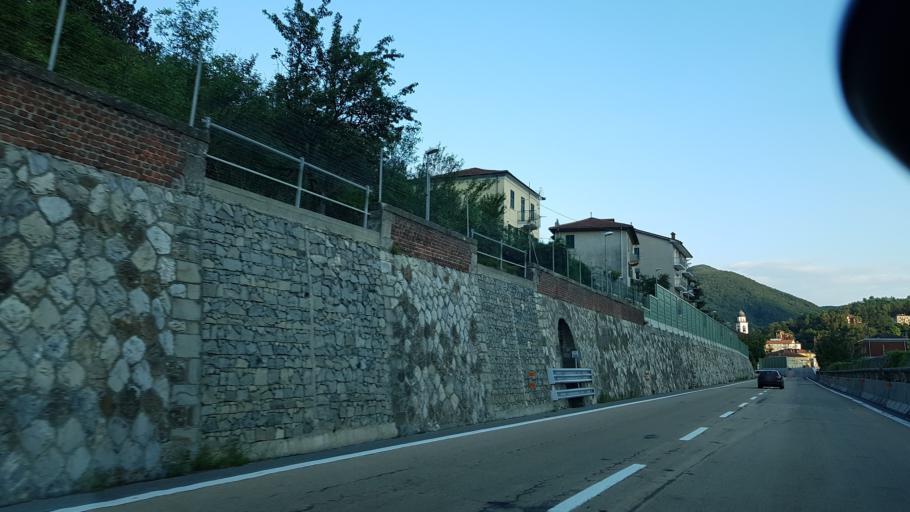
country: IT
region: Liguria
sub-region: Provincia di Genova
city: Ronco Scrivia
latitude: 44.6183
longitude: 8.9470
